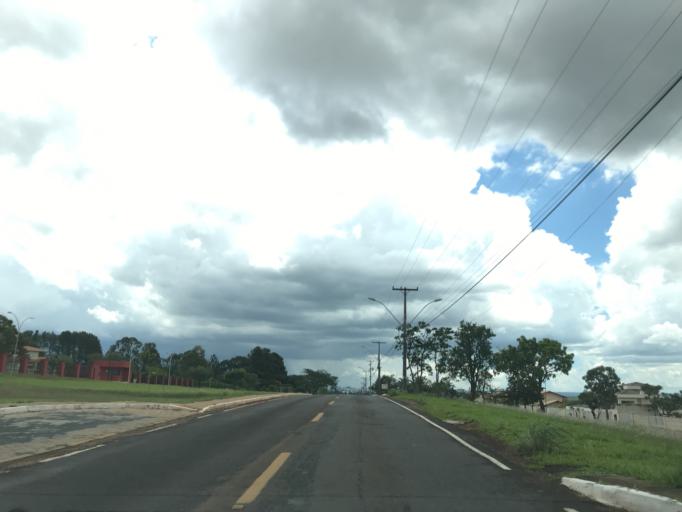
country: BR
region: Federal District
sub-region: Brasilia
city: Brasilia
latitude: -15.8953
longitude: -47.9126
